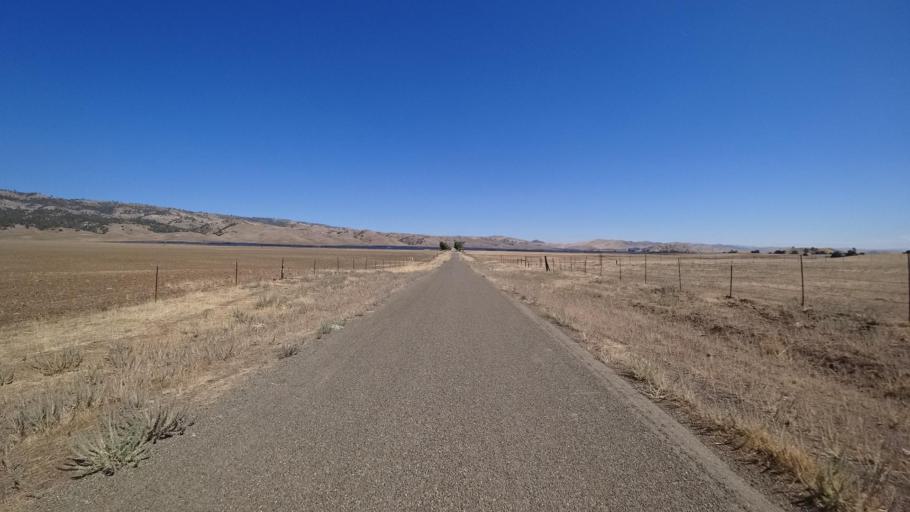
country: US
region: California
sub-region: San Luis Obispo County
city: Shandon
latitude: 35.8778
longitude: -120.3562
